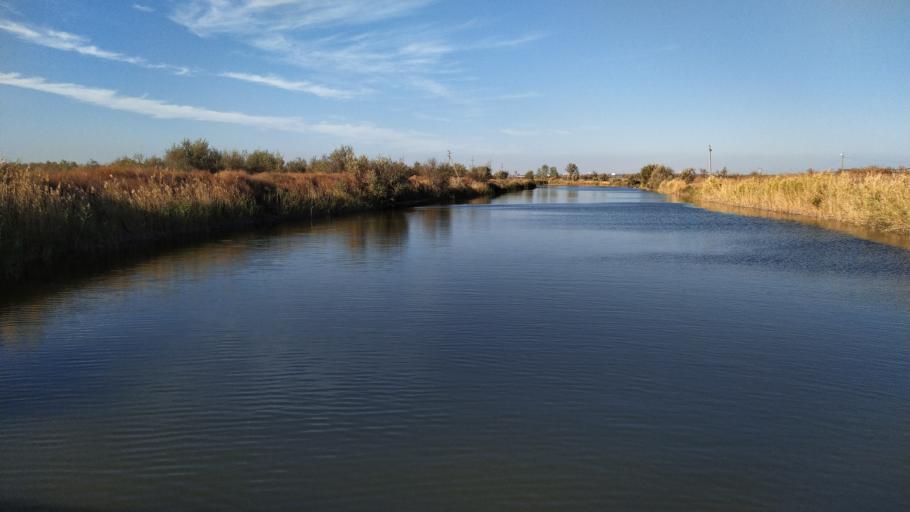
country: RU
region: Rostov
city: Kuleshovka
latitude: 47.1163
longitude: 39.6201
